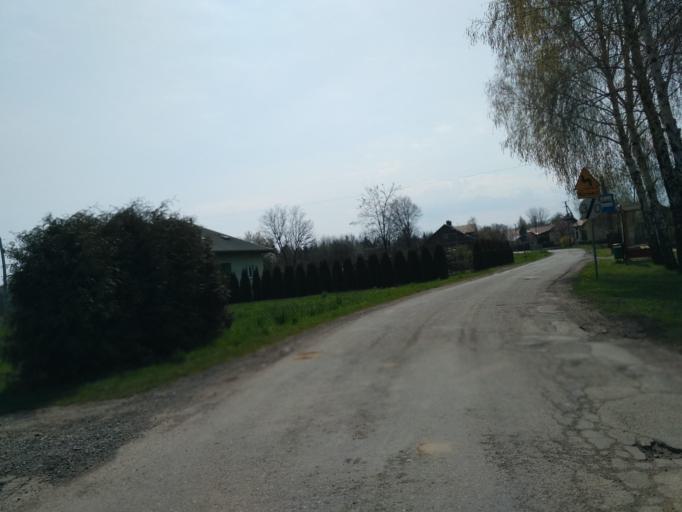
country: PL
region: Subcarpathian Voivodeship
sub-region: Powiat krosnienski
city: Chorkowka
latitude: 49.6388
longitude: 21.7247
